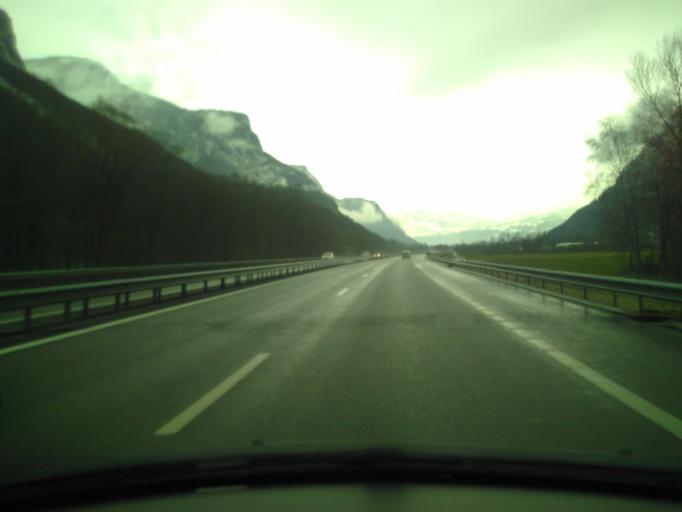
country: FR
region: Rhone-Alpes
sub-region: Departement de la Haute-Savoie
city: Magland
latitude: 46.0059
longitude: 6.6274
